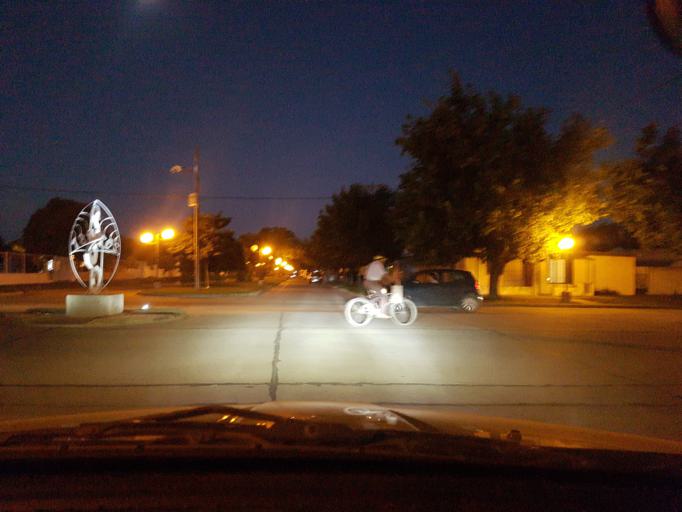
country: AR
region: Cordoba
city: Las Perdices
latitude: -32.7565
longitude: -63.7818
